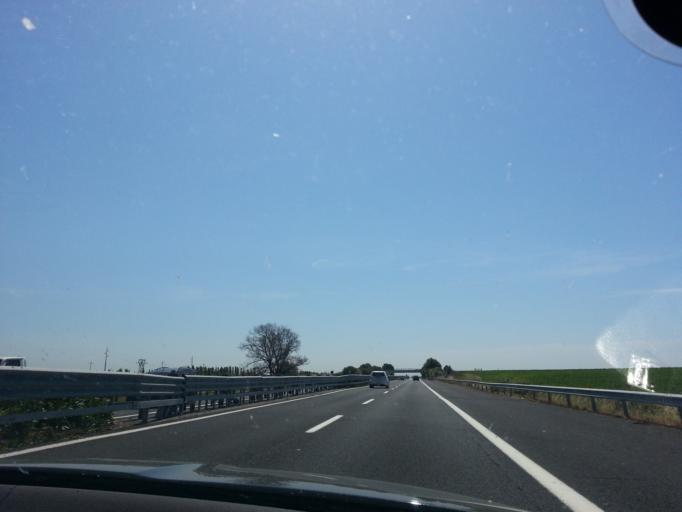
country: IT
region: Latium
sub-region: Citta metropolitana di Roma Capitale
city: Marina di Cerveteri
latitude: 42.0049
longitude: 12.0344
